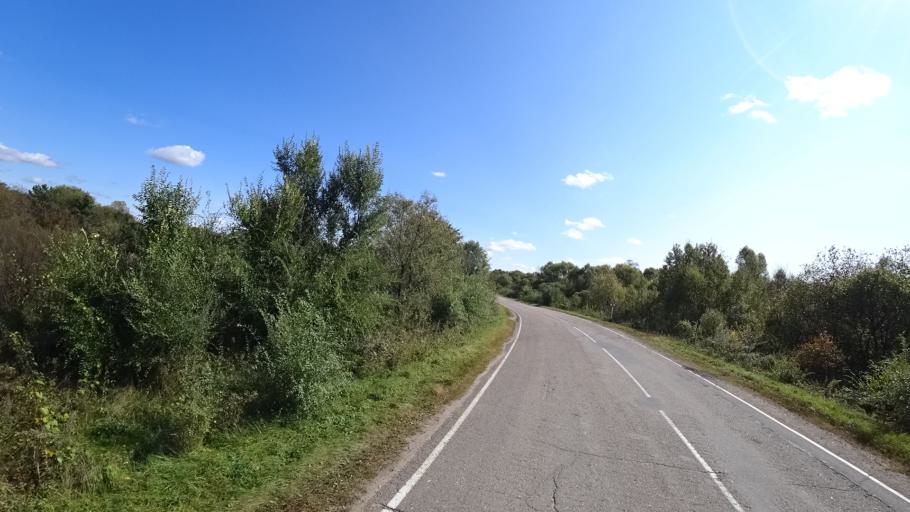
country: RU
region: Amur
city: Arkhara
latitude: 49.4014
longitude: 130.1299
